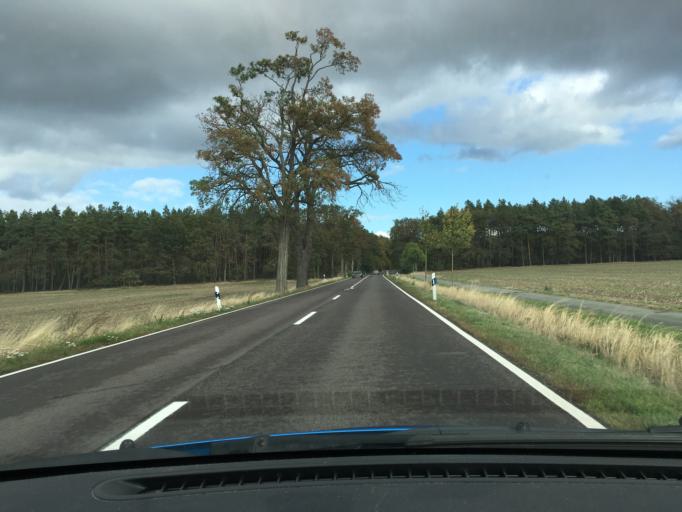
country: DE
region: Saxony-Anhalt
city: Pretzier
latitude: 52.8508
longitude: 11.3525
